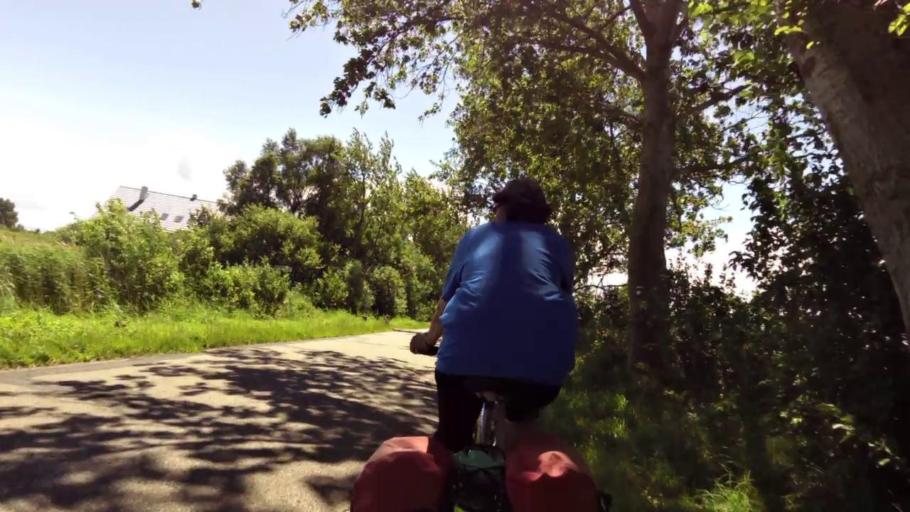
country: PL
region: West Pomeranian Voivodeship
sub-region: Powiat koszalinski
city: Sianow
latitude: 54.2900
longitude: 16.2104
